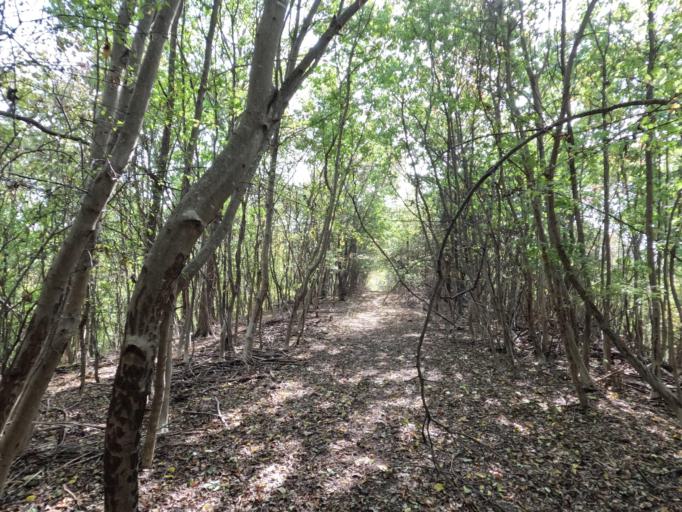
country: HU
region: Tolna
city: Szentgalpuszta
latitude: 46.3449
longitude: 18.6288
